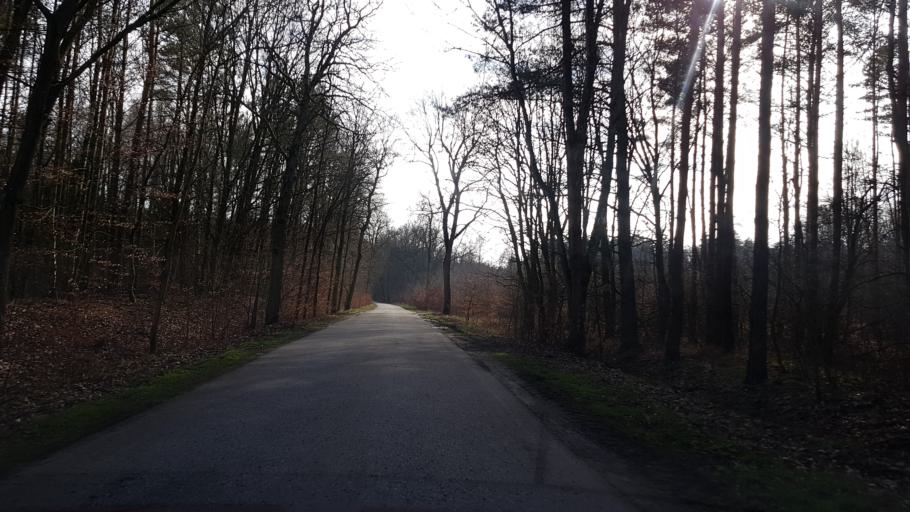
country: PL
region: West Pomeranian Voivodeship
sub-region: Powiat policki
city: Dobra
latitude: 53.5763
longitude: 14.3219
